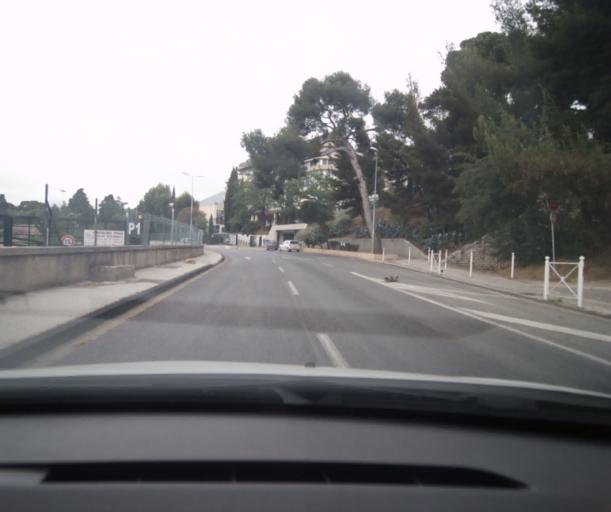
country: FR
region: Provence-Alpes-Cote d'Azur
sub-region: Departement du Var
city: Toulon
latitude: 43.1285
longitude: 5.9346
